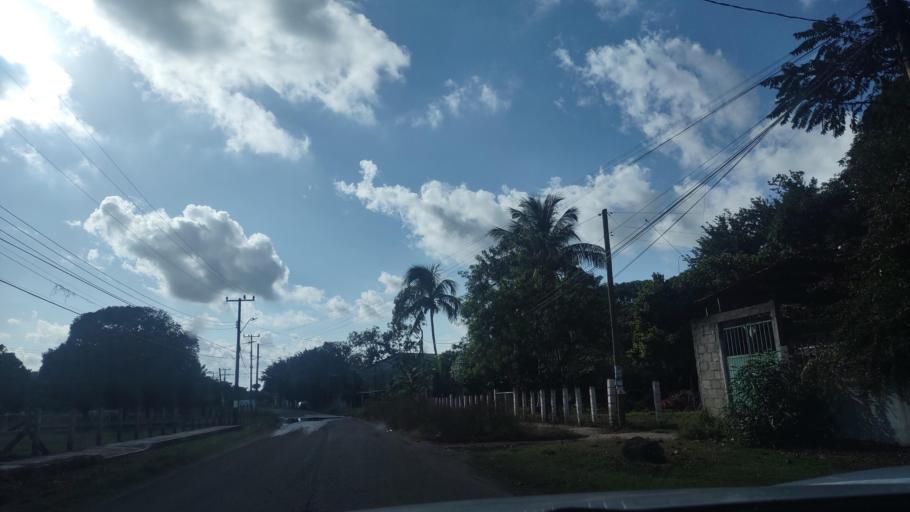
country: MX
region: Veracruz
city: El Tejar
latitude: 19.0710
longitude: -96.1657
